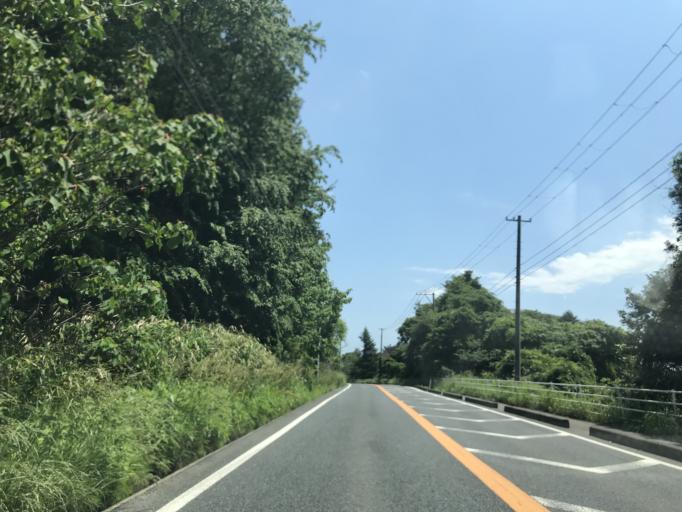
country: JP
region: Miyagi
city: Matsushima
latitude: 38.3896
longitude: 141.1082
